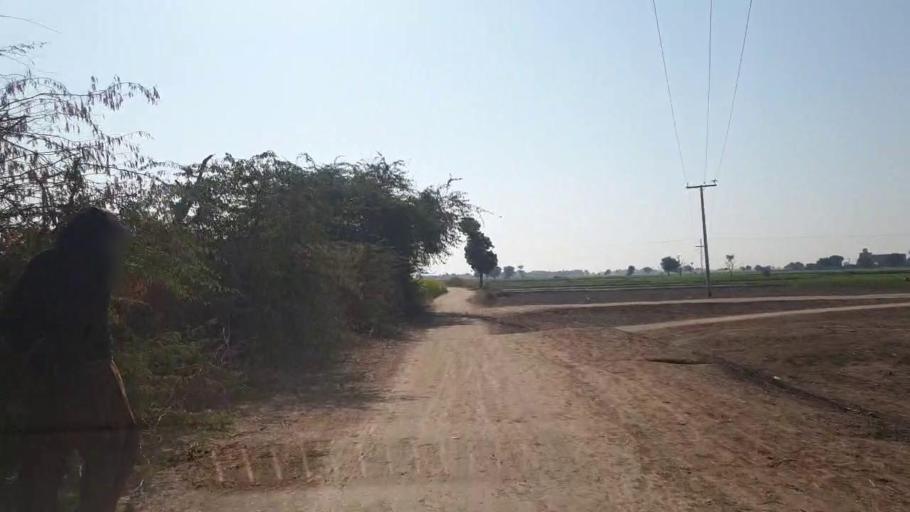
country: PK
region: Sindh
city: Shahpur Chakar
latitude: 26.0757
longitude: 68.6426
